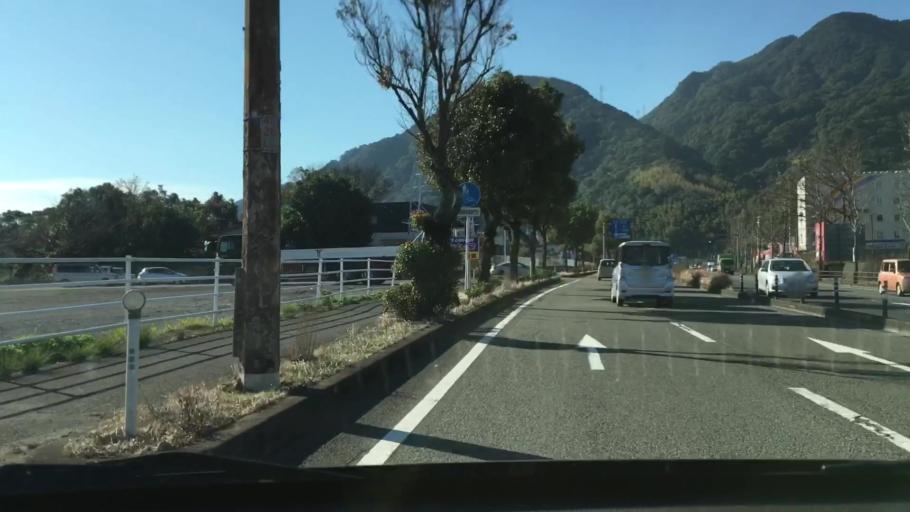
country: JP
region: Kagoshima
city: Kajiki
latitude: 31.7079
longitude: 130.6147
